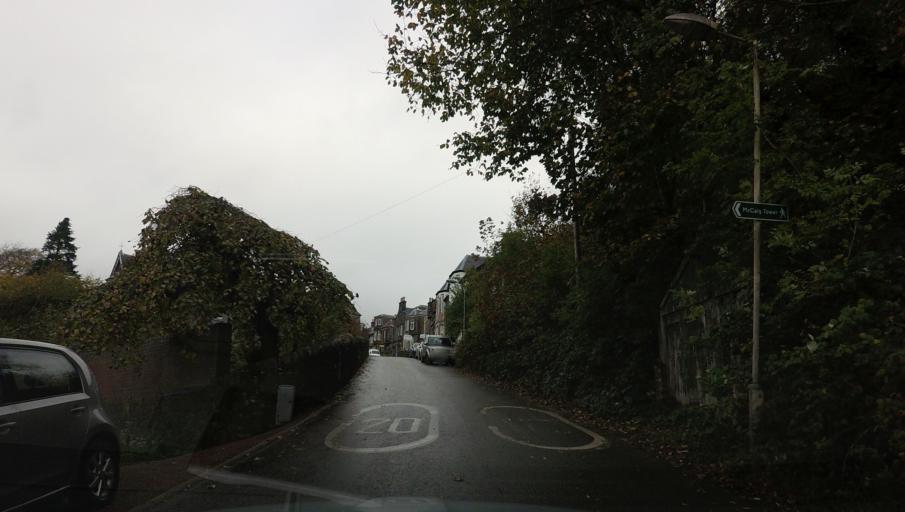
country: GB
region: Scotland
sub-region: Argyll and Bute
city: Oban
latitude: 56.4130
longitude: -5.4689
